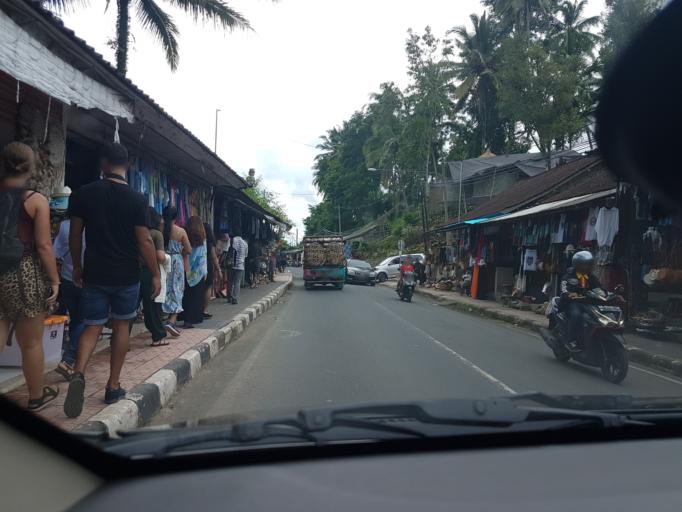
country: ID
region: Bali
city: Tegalalang
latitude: -8.4341
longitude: 115.2787
